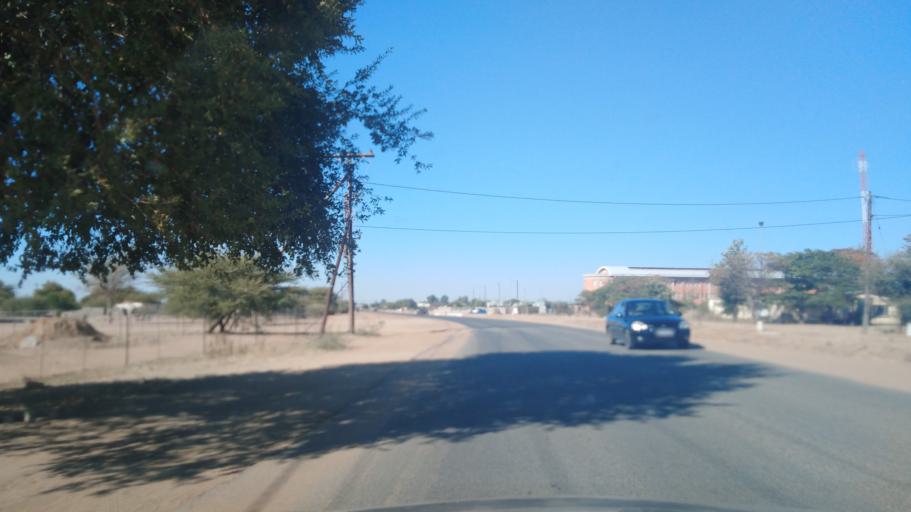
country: BW
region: Central
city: Mahalapye
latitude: -23.1194
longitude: 26.7939
